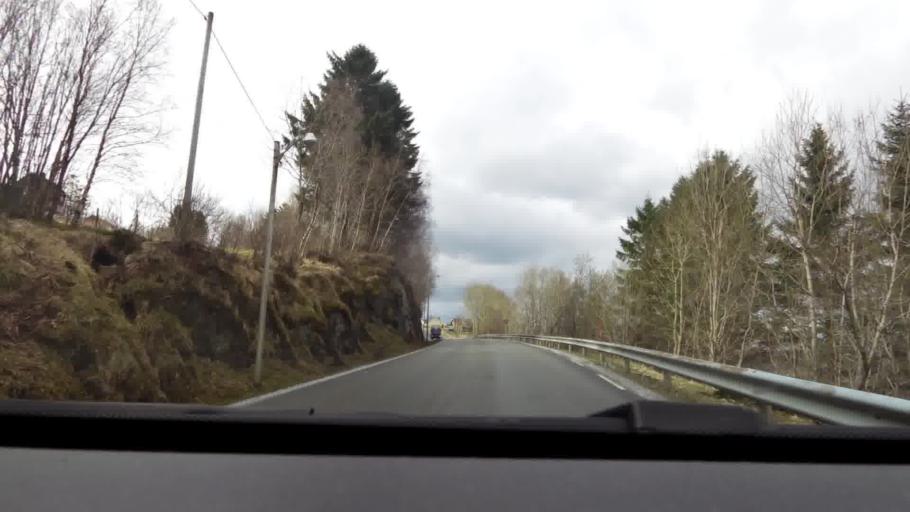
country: NO
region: More og Romsdal
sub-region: Gjemnes
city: Batnfjordsora
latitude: 62.9248
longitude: 7.5763
